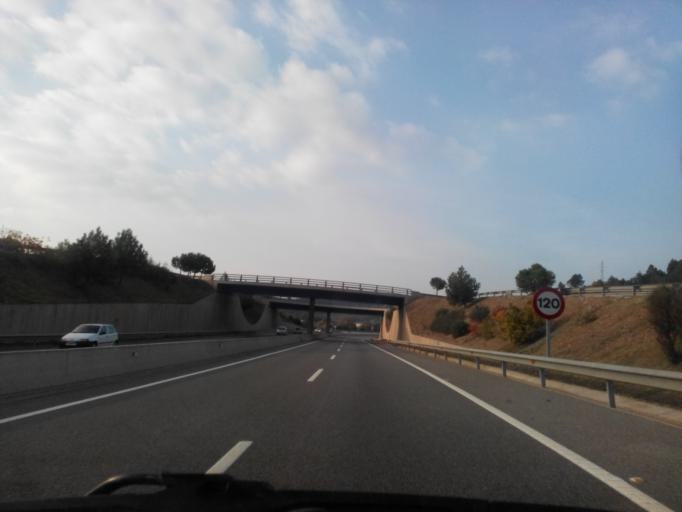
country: ES
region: Catalonia
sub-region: Provincia de Barcelona
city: Sallent
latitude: 41.8330
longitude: 1.8836
